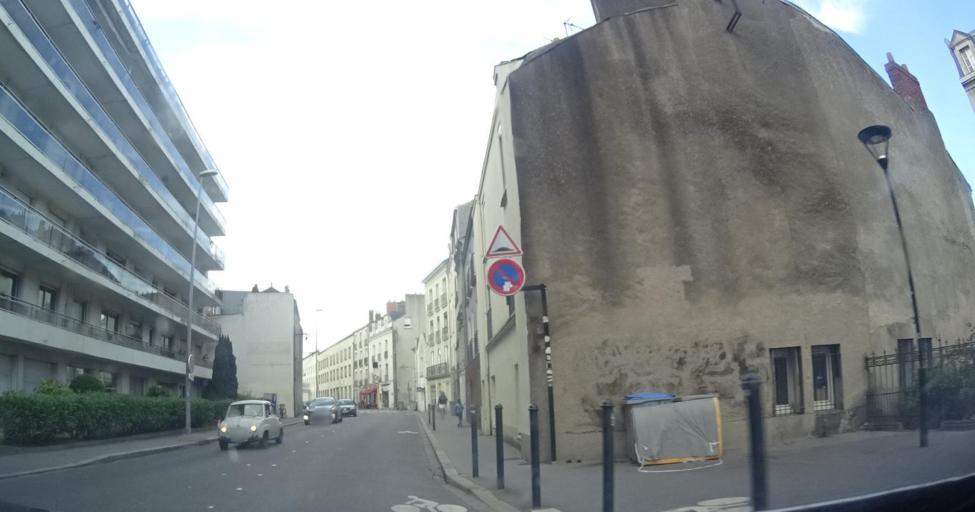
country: FR
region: Pays de la Loire
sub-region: Departement de la Loire-Atlantique
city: Nantes
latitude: 47.2223
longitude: -1.5466
